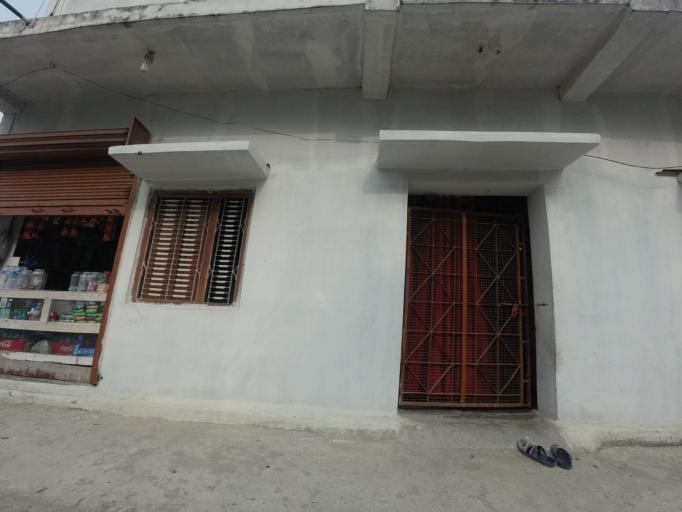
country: NP
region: Western Region
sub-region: Lumbini Zone
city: Bhairahawa
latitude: 27.4948
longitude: 83.4512
